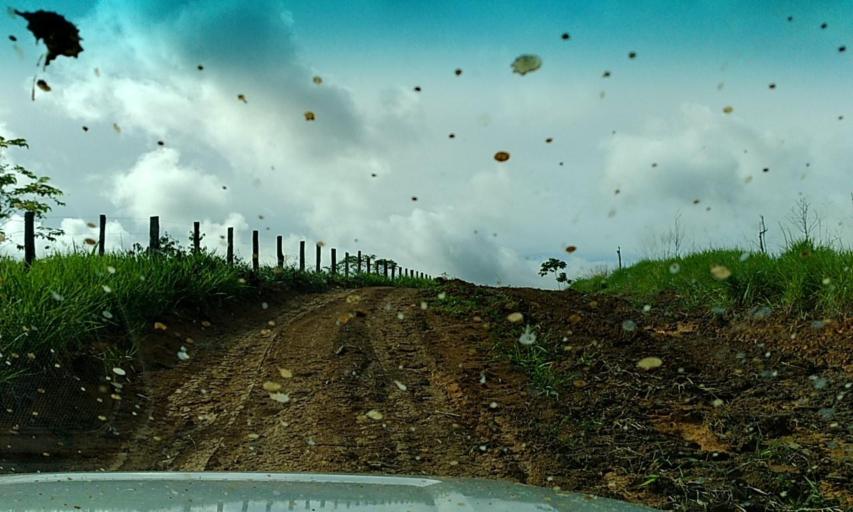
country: BR
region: Para
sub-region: Senador Jose Porfirio
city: Senador Jose Porfirio
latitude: -3.0020
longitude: -51.7394
